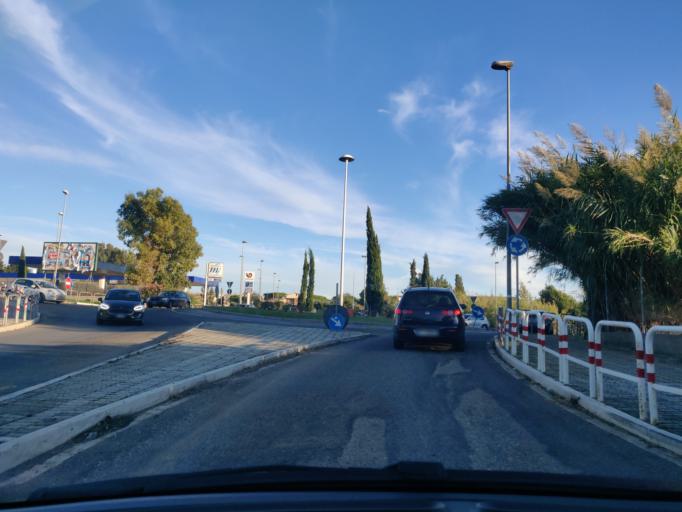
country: IT
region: Latium
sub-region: Citta metropolitana di Roma Capitale
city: Civitavecchia
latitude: 42.1011
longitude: 11.7947
